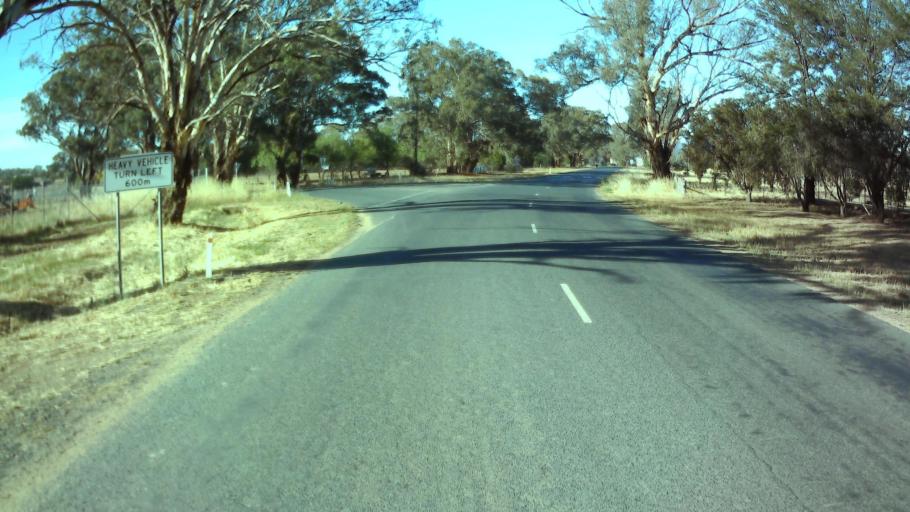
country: AU
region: New South Wales
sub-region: Weddin
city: Grenfell
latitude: -33.9012
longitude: 148.1518
